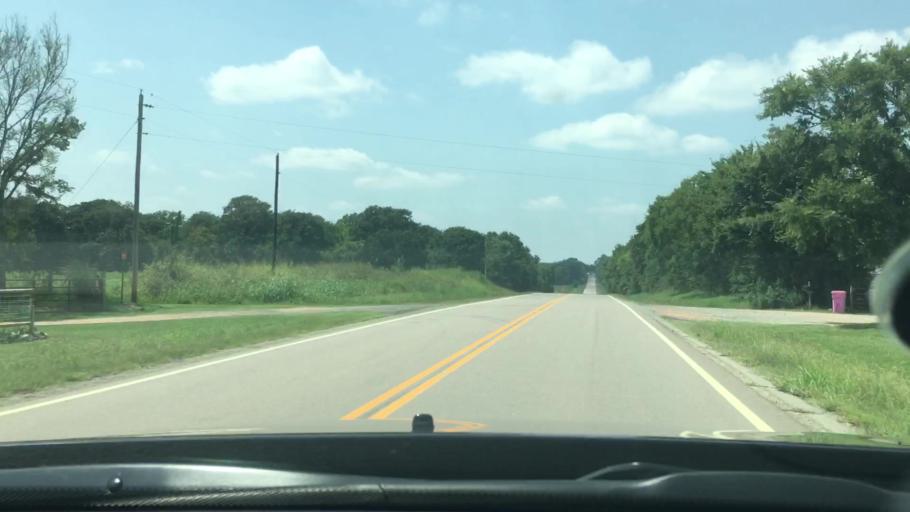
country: US
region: Oklahoma
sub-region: Coal County
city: Coalgate
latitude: 34.3698
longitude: -96.3460
